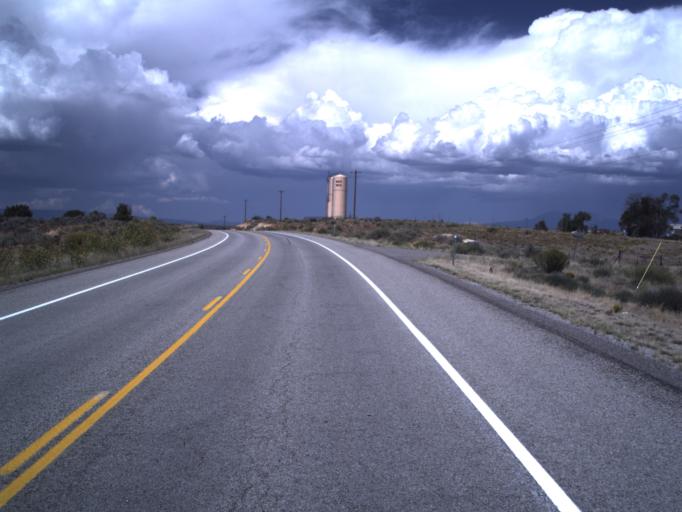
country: US
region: Utah
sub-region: San Juan County
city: Blanding
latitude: 37.4789
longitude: -109.4685
